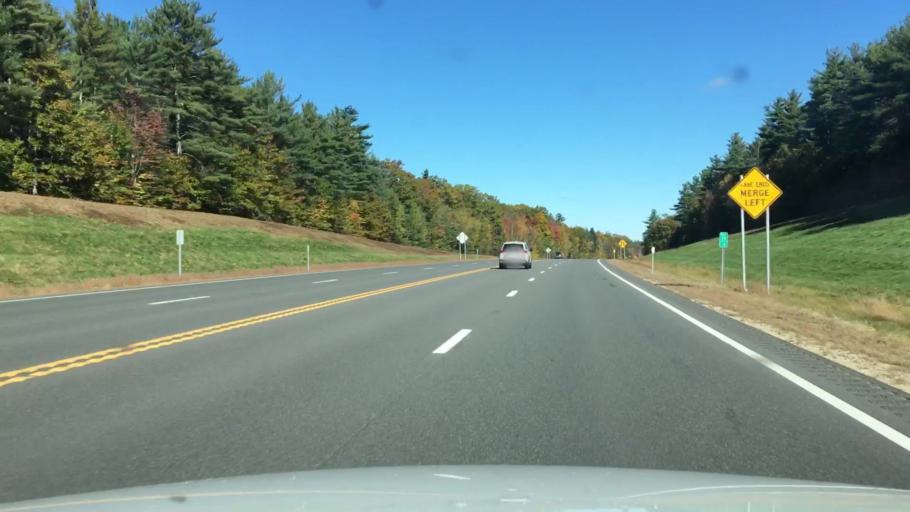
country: US
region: New Hampshire
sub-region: Strafford County
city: Farmington
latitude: 43.4301
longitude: -71.0094
